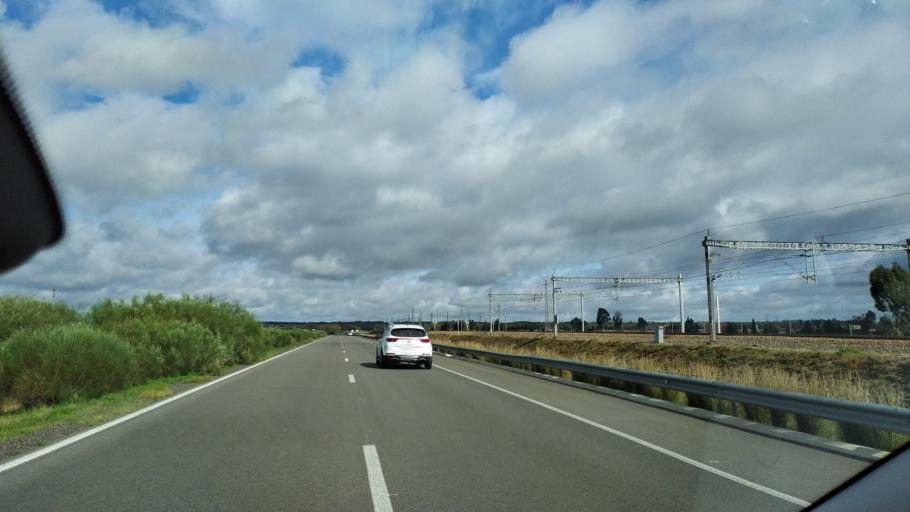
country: MA
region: Gharb-Chrarda-Beni Hssen
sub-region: Kenitra Province
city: Lalla Mimouna
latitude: 34.8929
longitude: -6.2097
